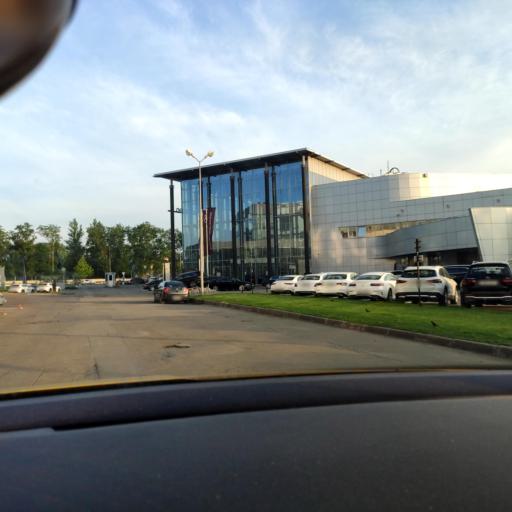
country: RU
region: Moskovskaya
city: Reutov
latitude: 55.7853
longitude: 37.8706
